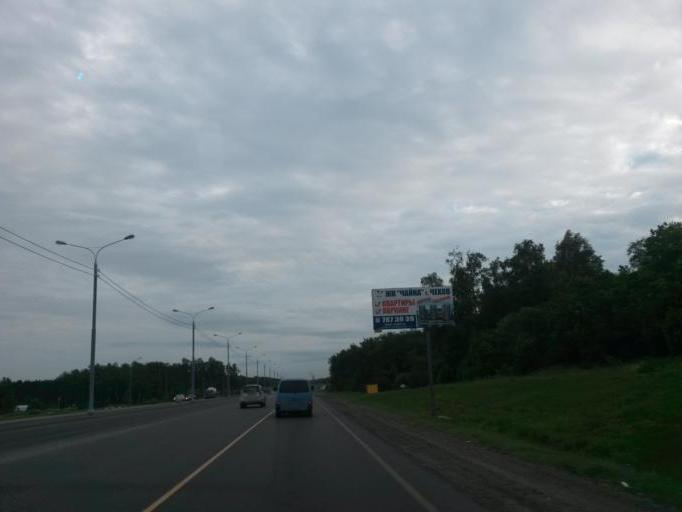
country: RU
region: Moskovskaya
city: L'vovskiy
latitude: 55.3192
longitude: 37.5573
